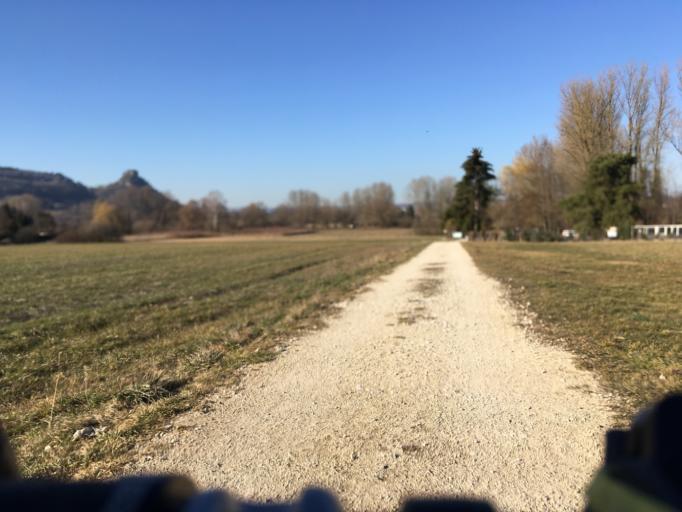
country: DE
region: Baden-Wuerttemberg
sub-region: Freiburg Region
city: Singen
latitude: 47.7806
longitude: 8.8395
